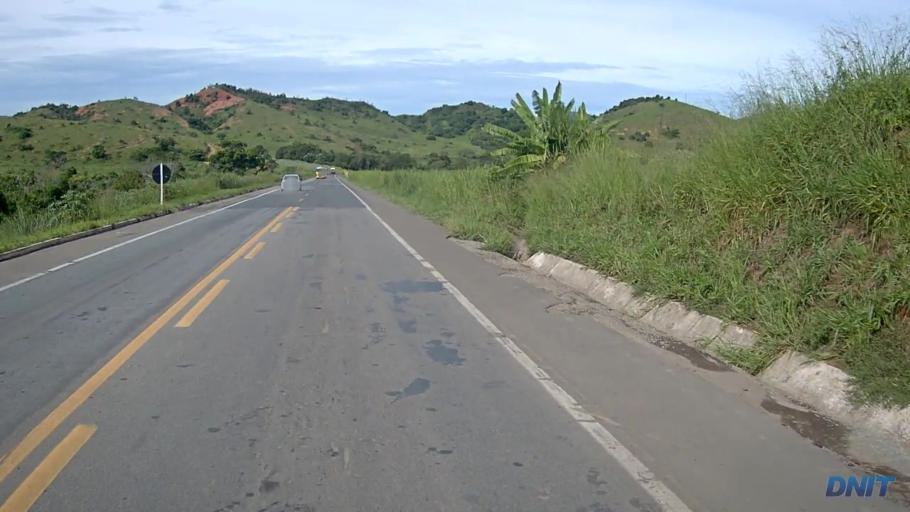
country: BR
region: Minas Gerais
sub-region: Belo Oriente
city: Belo Oriente
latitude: -19.2207
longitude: -42.3113
